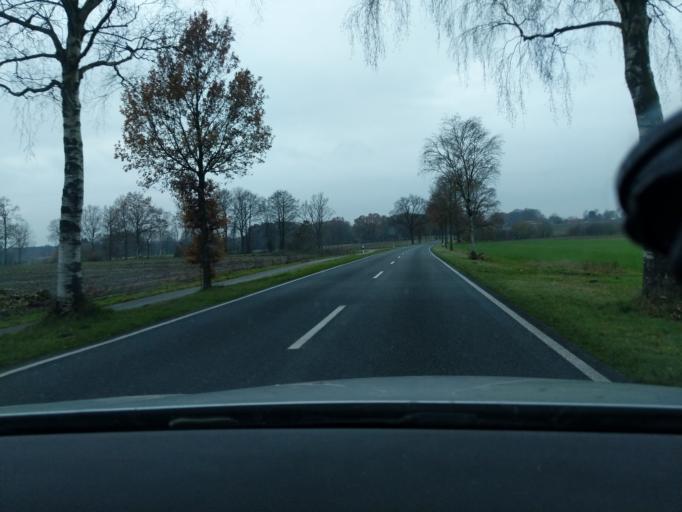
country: DE
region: Lower Saxony
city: Heeslingen
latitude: 53.3413
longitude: 9.3864
